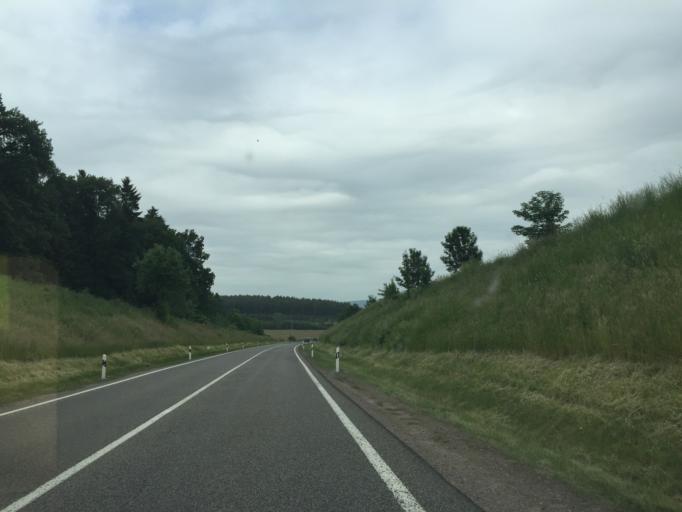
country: DE
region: Thuringia
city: Langewiesen
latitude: 50.7084
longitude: 10.9645
